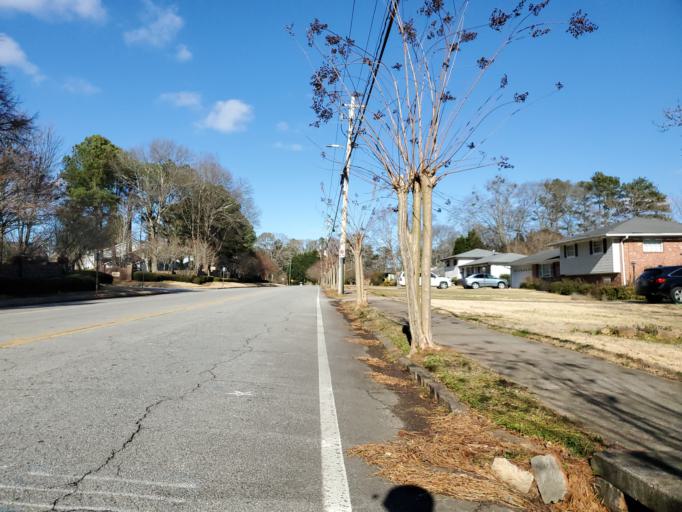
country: US
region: Georgia
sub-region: DeKalb County
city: Belvedere Park
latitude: 33.7622
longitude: -84.2673
